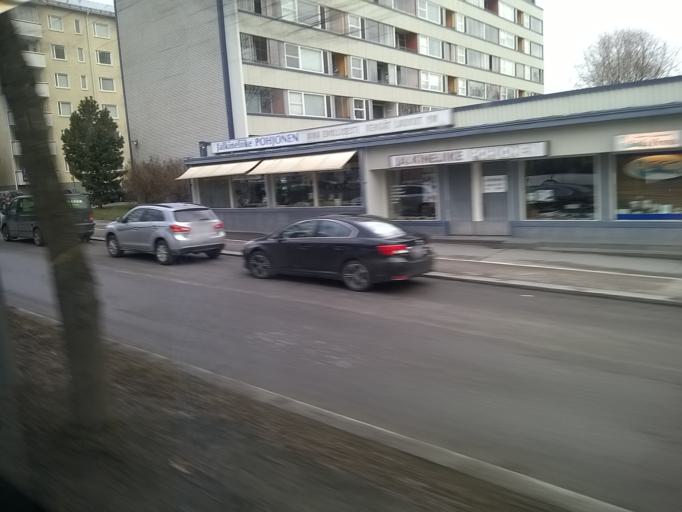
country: FI
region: Pirkanmaa
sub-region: Tampere
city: Tampere
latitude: 61.4959
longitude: 23.8066
